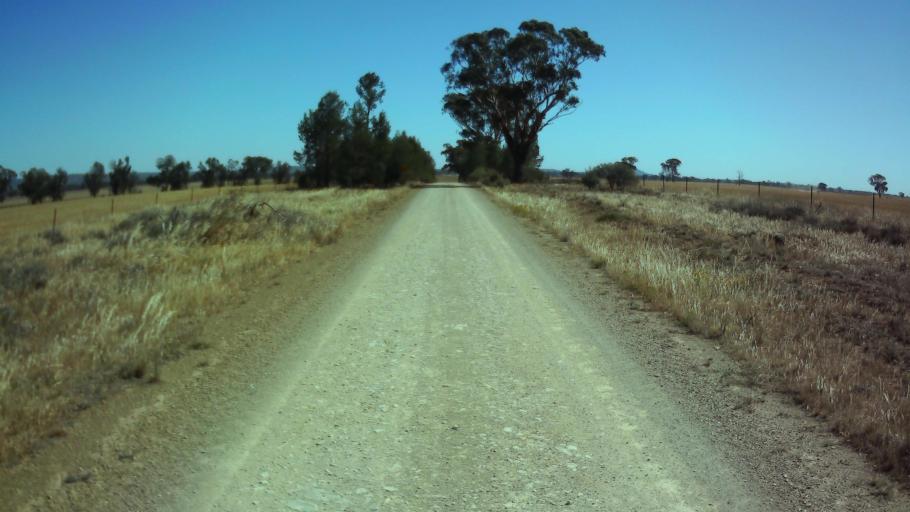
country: AU
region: New South Wales
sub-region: Weddin
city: Grenfell
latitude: -33.8764
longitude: 147.8740
